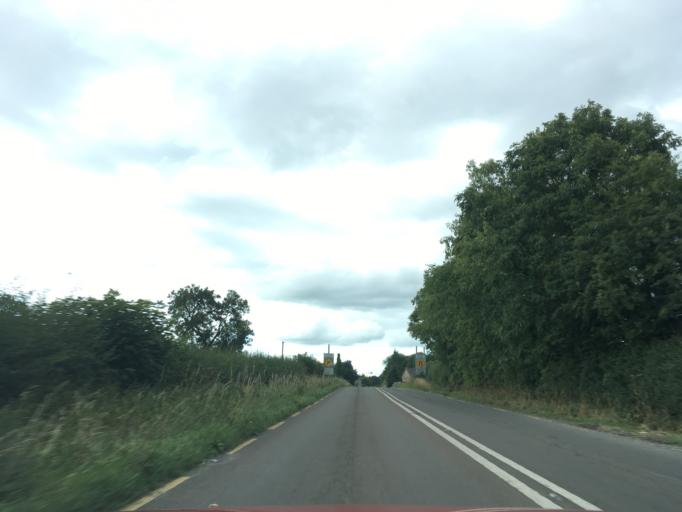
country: IE
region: Munster
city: Cahir
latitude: 52.4300
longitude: -7.8866
